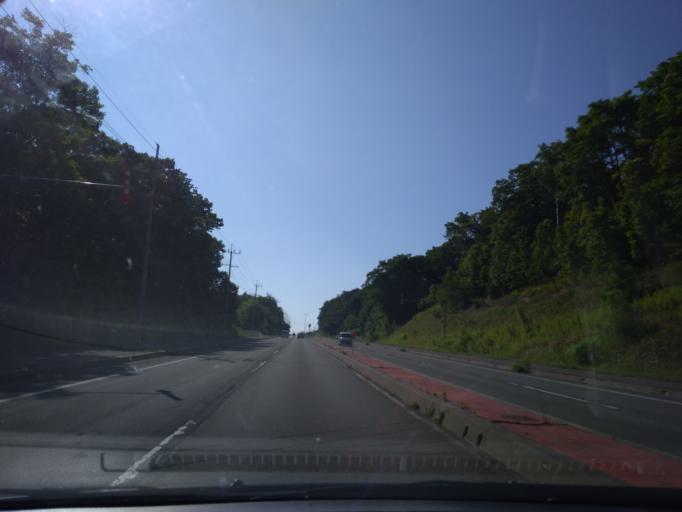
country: JP
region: Hokkaido
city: Kitahiroshima
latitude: 42.9783
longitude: 141.5074
